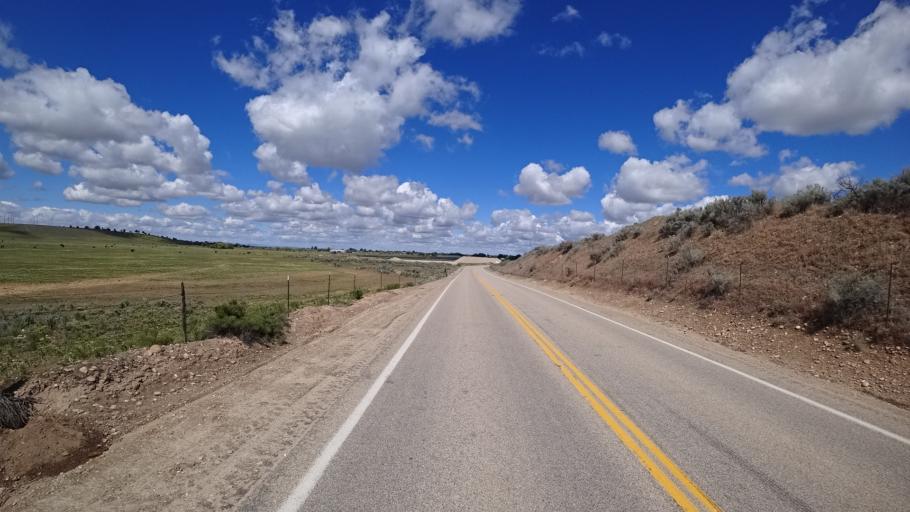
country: US
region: Idaho
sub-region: Ada County
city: Kuna
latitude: 43.5098
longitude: -116.3111
